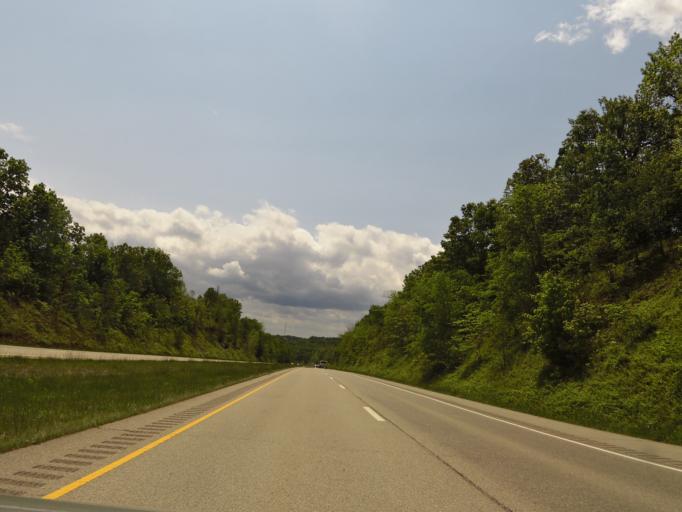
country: US
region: Ohio
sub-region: Meigs County
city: Pomeroy
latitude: 39.0865
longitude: -82.0163
